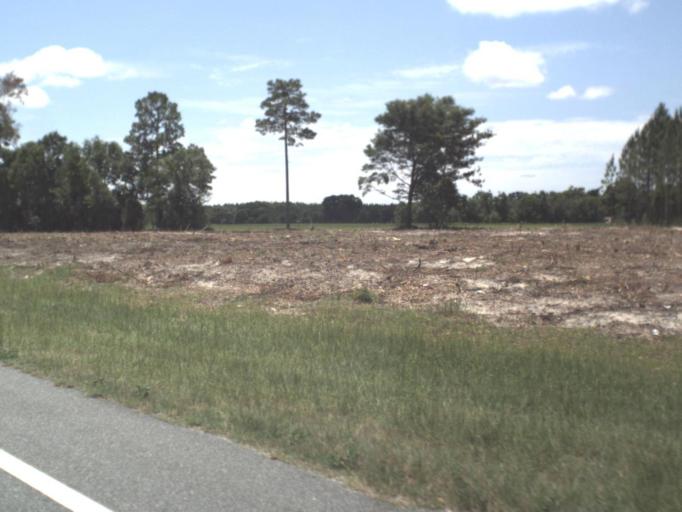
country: US
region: Florida
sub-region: Lafayette County
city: Mayo
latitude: 29.8666
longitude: -82.9587
